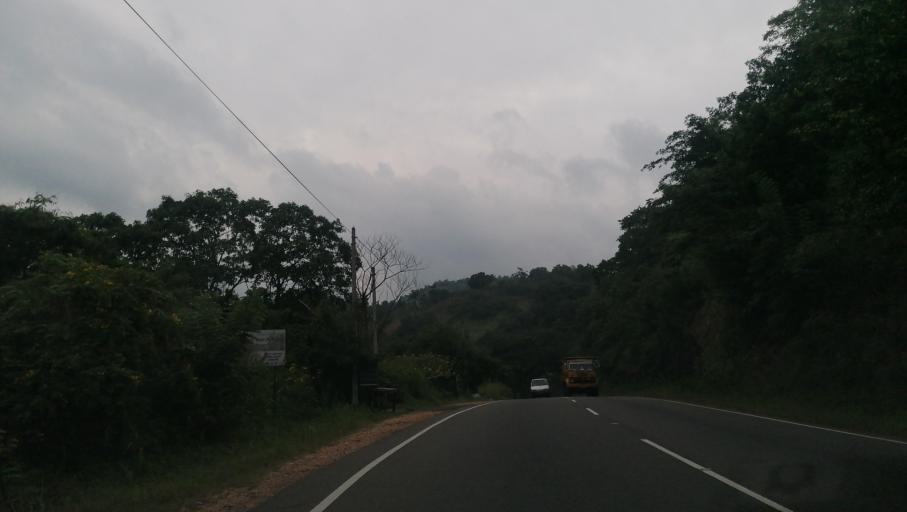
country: LK
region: Central
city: Kandy
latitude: 7.2413
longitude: 80.7256
